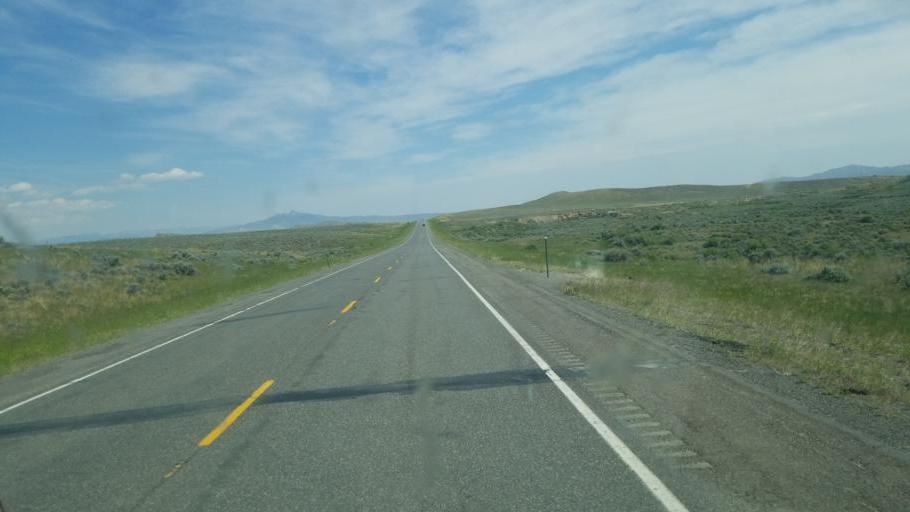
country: US
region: Wyoming
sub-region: Park County
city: Cody
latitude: 44.4214
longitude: -109.0098
